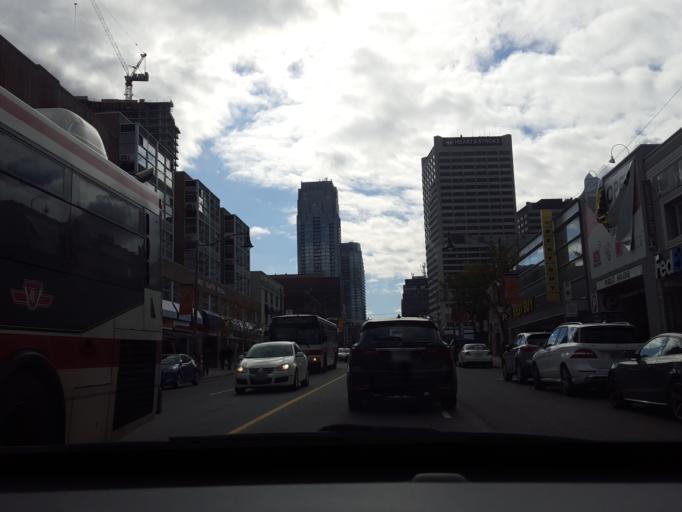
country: CA
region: Ontario
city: Toronto
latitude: 43.7106
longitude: -79.3992
